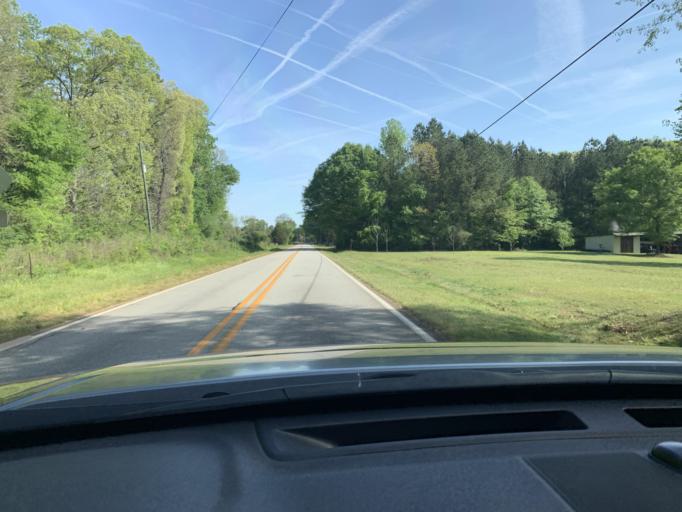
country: US
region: Georgia
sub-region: Oconee County
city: Watkinsville
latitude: 33.7987
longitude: -83.3198
